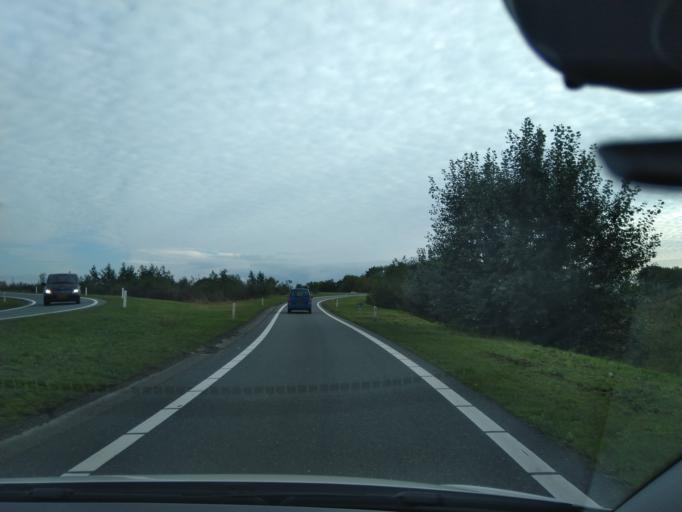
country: NL
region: Groningen
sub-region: Gemeente Veendam
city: Veendam
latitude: 53.0979
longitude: 6.8937
